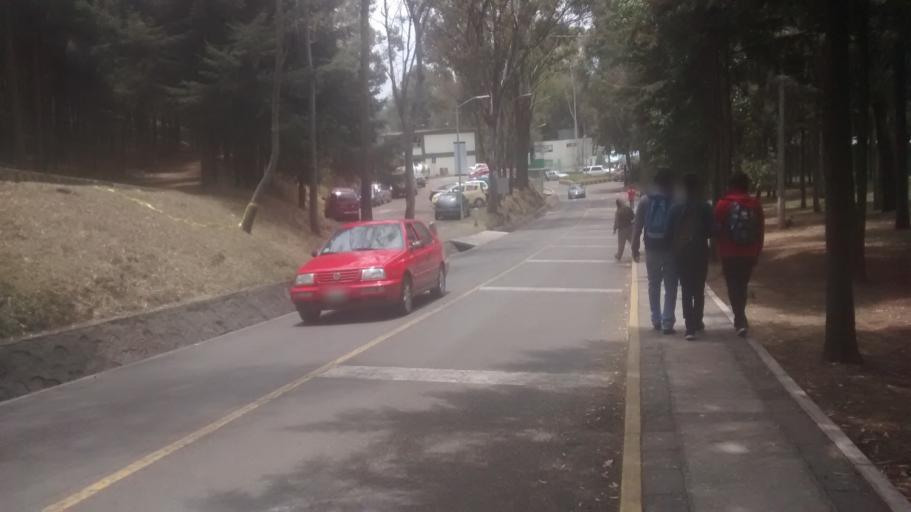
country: MX
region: Mexico
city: San Buenaventura
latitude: 19.2848
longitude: -99.6797
